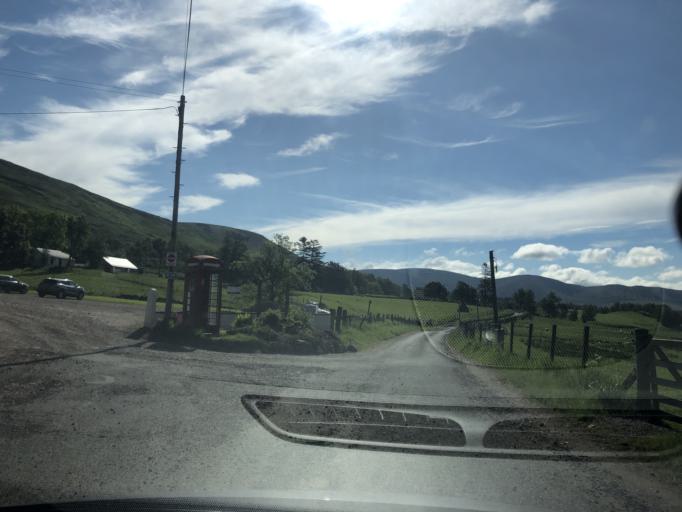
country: GB
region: Scotland
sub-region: Angus
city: Kirriemuir
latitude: 56.8441
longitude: -3.1041
